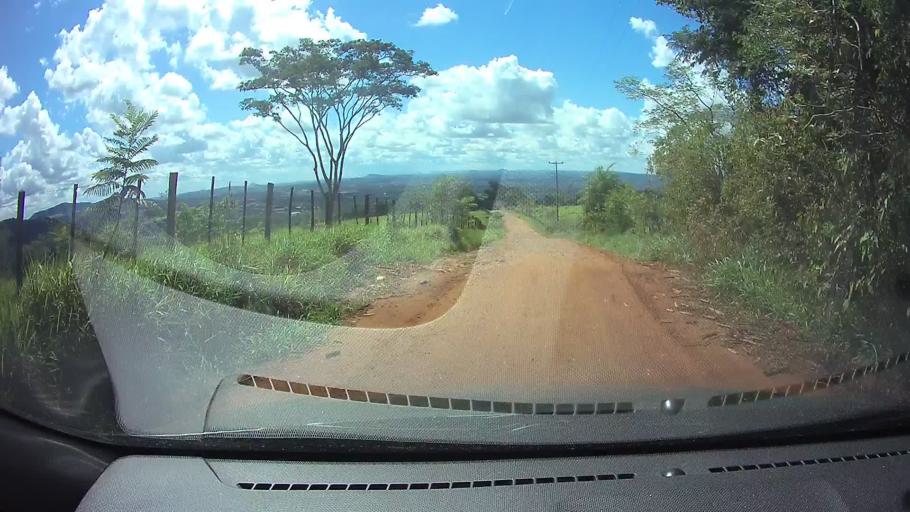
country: PY
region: Paraguari
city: La Colmena
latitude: -25.9401
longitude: -56.7797
